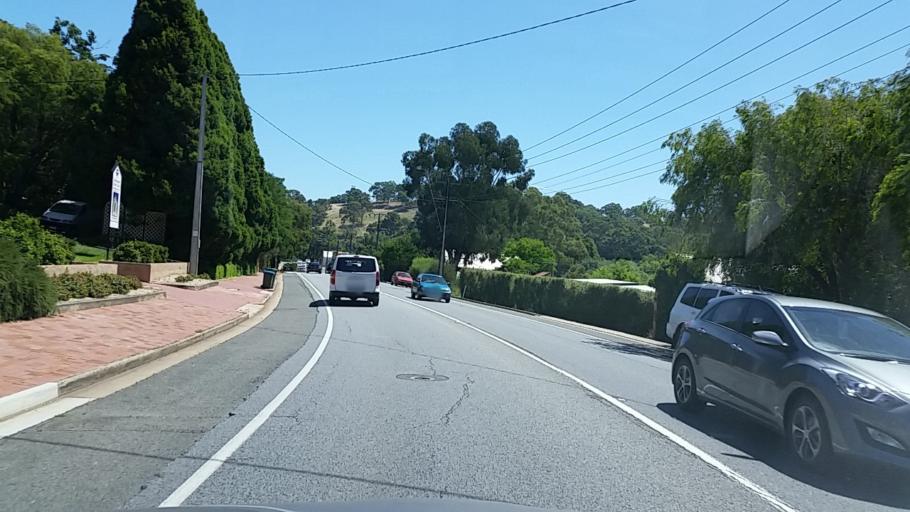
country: AU
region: South Australia
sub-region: Mount Barker
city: Little Hampton
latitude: -35.0489
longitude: 138.8623
